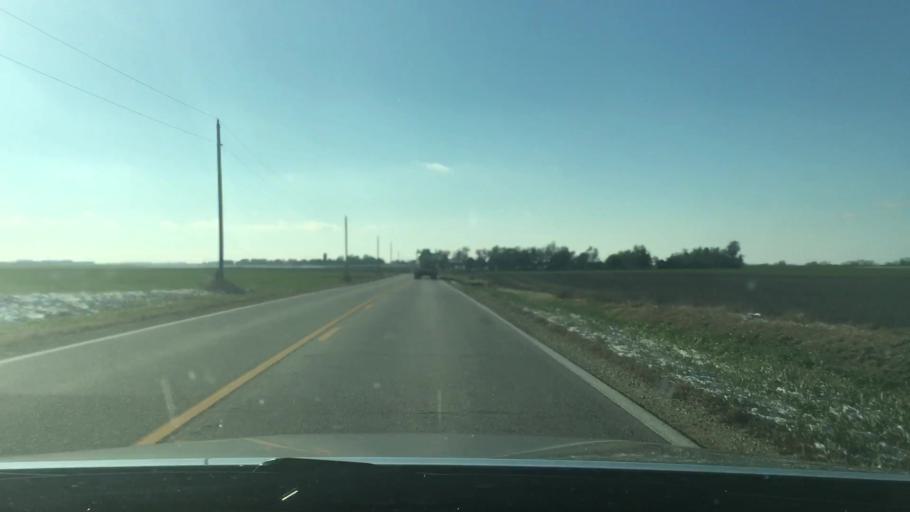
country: US
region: Kansas
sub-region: Rice County
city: Sterling
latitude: 38.1448
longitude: -98.1674
